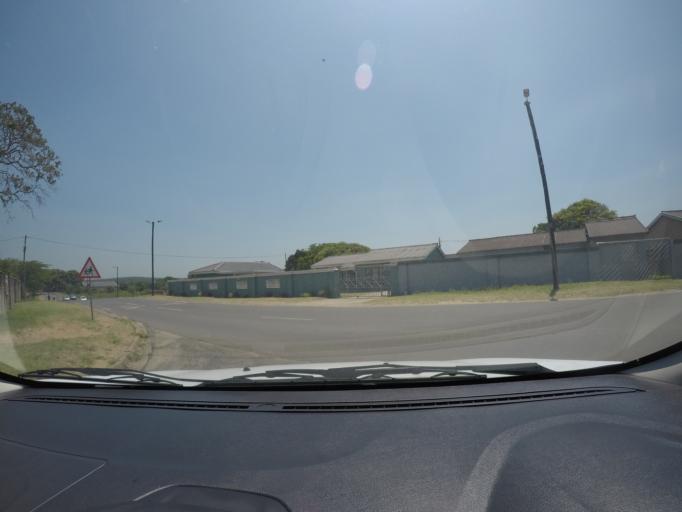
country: ZA
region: KwaZulu-Natal
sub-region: uThungulu District Municipality
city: eSikhawini
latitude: -28.8732
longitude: 31.9137
